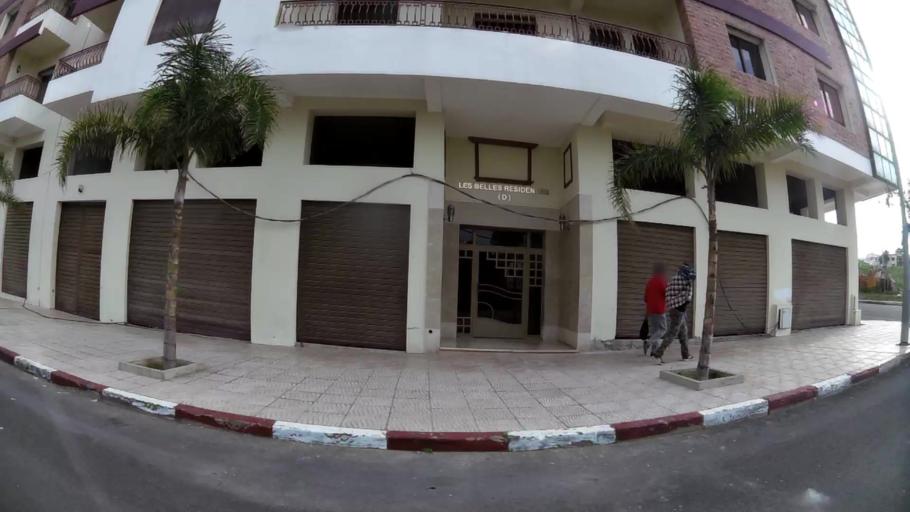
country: MA
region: Tanger-Tetouan
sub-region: Tanger-Assilah
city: Tangier
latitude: 35.7704
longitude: -5.7909
